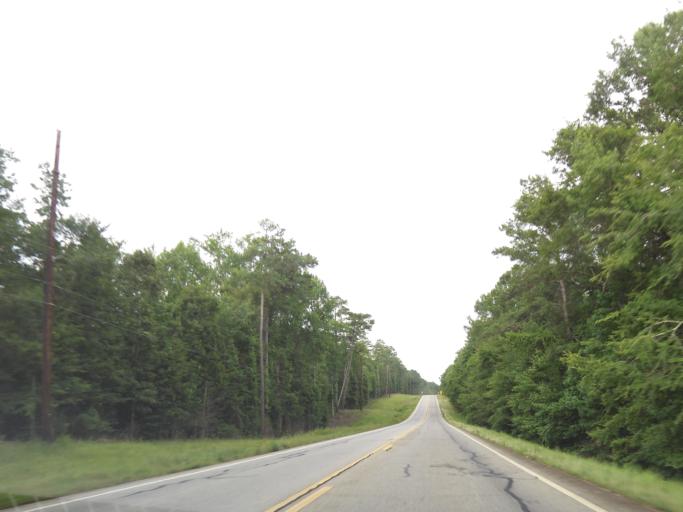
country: US
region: Georgia
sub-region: Bibb County
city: West Point
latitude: 32.8649
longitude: -83.8179
